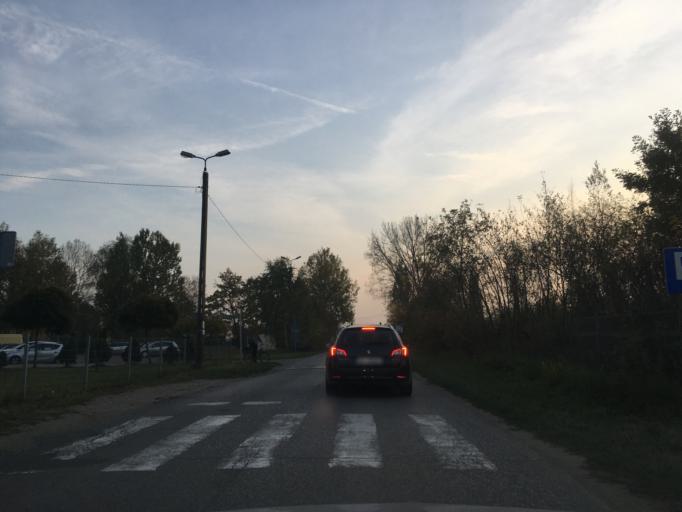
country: PL
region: Masovian Voivodeship
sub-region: Powiat piaseczynski
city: Lesznowola
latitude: 52.0700
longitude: 20.8938
